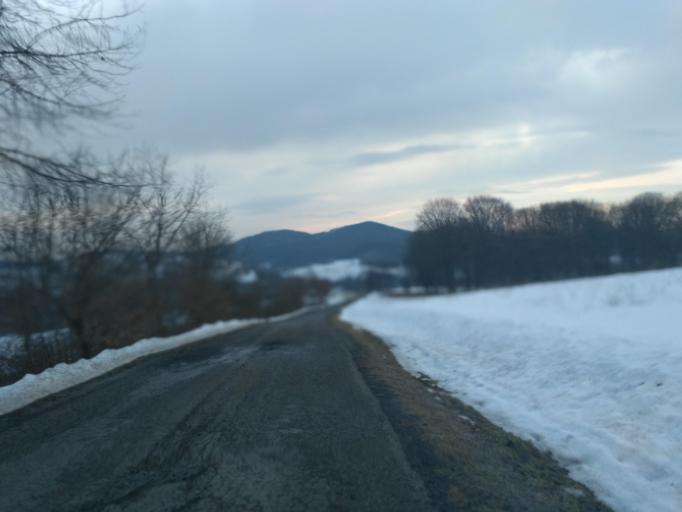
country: PL
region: Subcarpathian Voivodeship
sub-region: Powiat brzozowski
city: Dydnia
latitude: 49.6415
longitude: 22.1620
